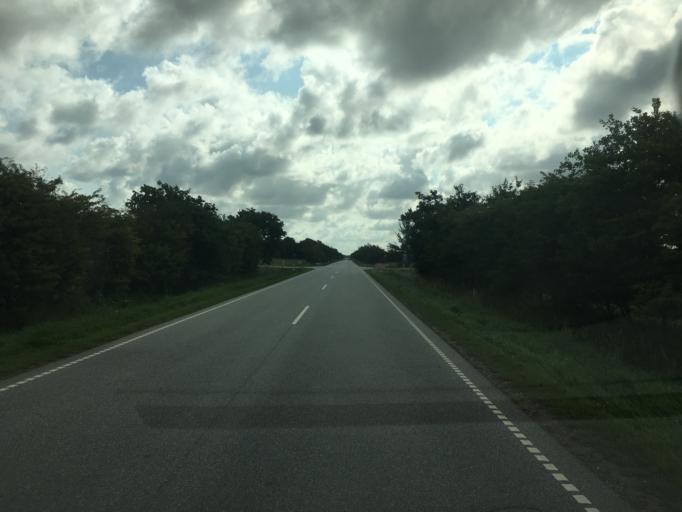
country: DK
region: South Denmark
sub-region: Tonder Kommune
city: Sherrebek
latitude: 55.1261
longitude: 8.8112
